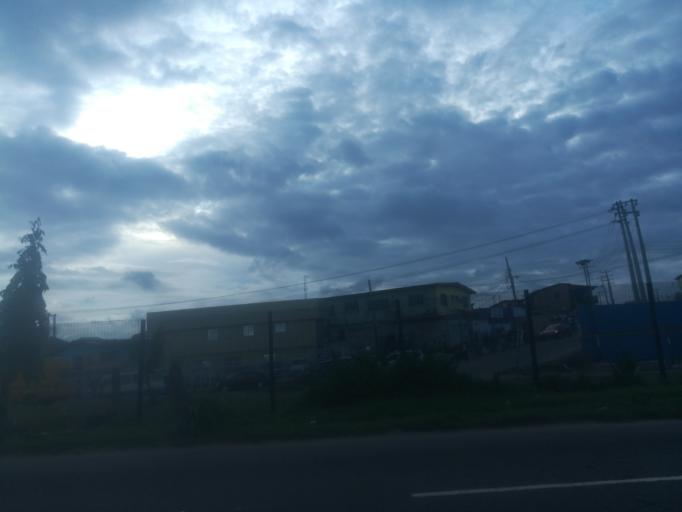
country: NG
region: Lagos
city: Ojota
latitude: 6.5716
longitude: 3.3974
